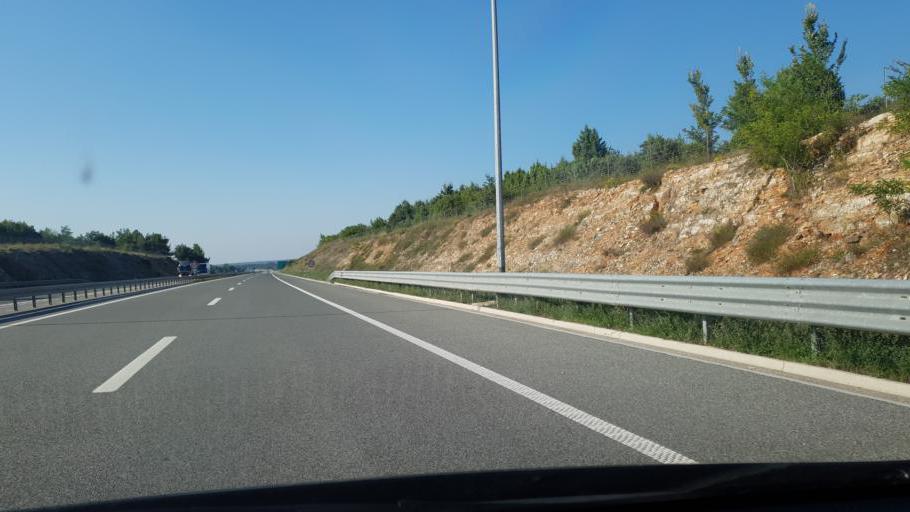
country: HR
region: Istarska
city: Vodnjan
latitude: 44.9559
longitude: 13.8721
